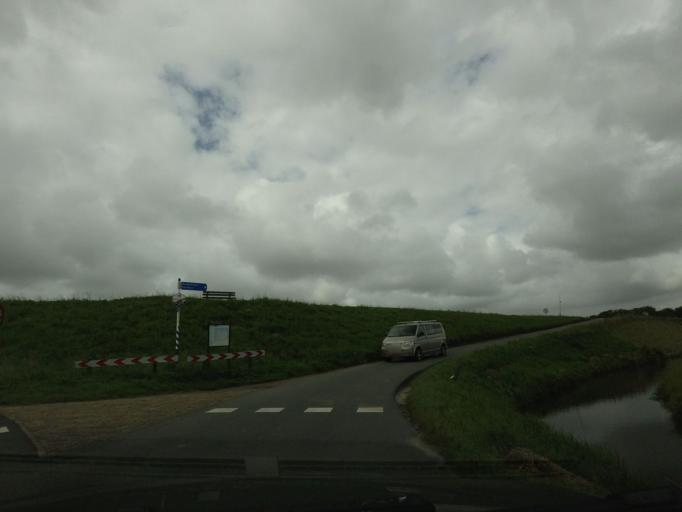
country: NL
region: North Holland
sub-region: Gemeente Schagen
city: Harenkarspel
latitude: 52.7408
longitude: 4.7160
